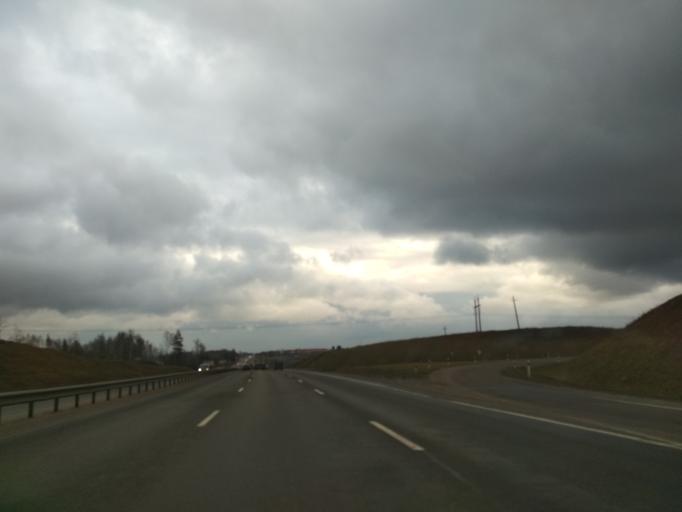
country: BY
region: Minsk
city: Pryvol'ny
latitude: 53.8137
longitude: 27.7750
